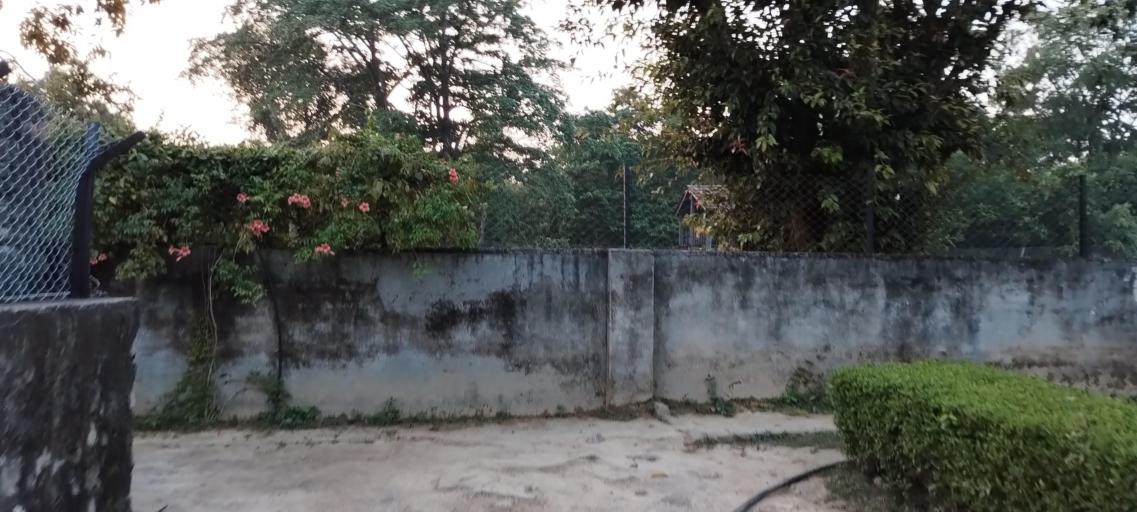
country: NP
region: Far Western
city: Tikapur
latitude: 28.4536
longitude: 81.2419
